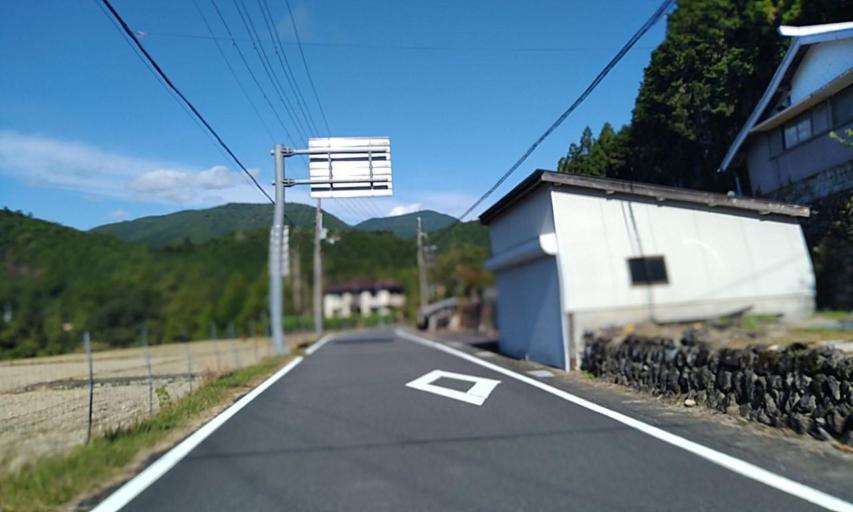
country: JP
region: Wakayama
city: Shingu
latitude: 33.9277
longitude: 135.9801
